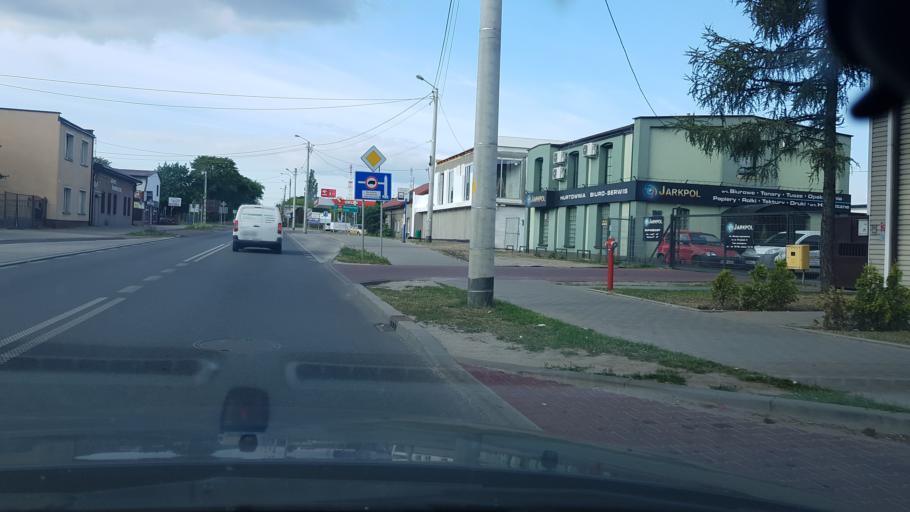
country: PL
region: Lodz Voivodeship
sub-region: Powiat tomaszowski
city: Tomaszow Mazowiecki
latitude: 51.5524
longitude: 20.0172
